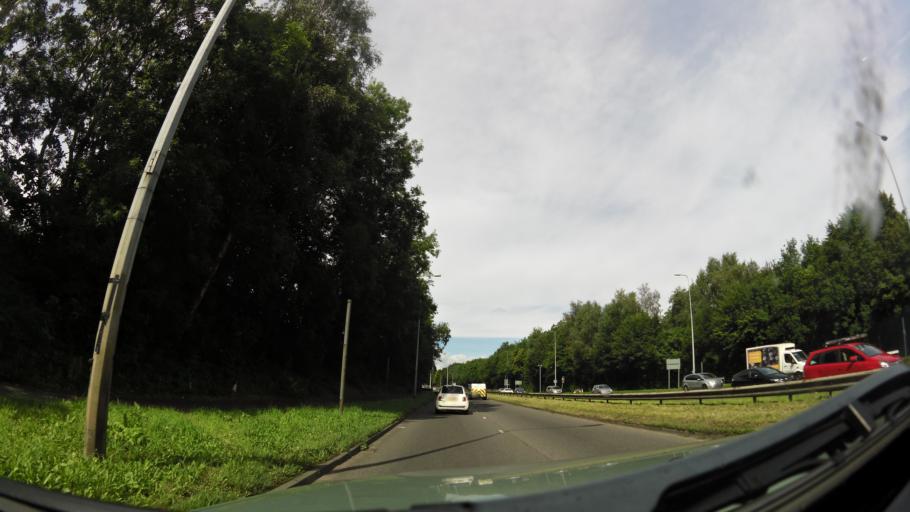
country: GB
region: Wales
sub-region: Cardiff
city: Radyr
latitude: 51.5242
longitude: -3.2306
